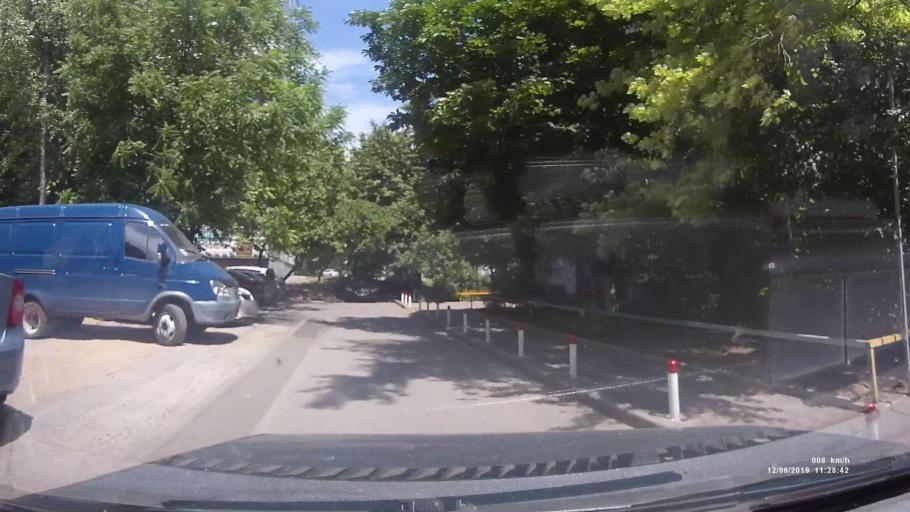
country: RU
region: Rostov
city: Severnyy
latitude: 47.2923
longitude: 39.7123
